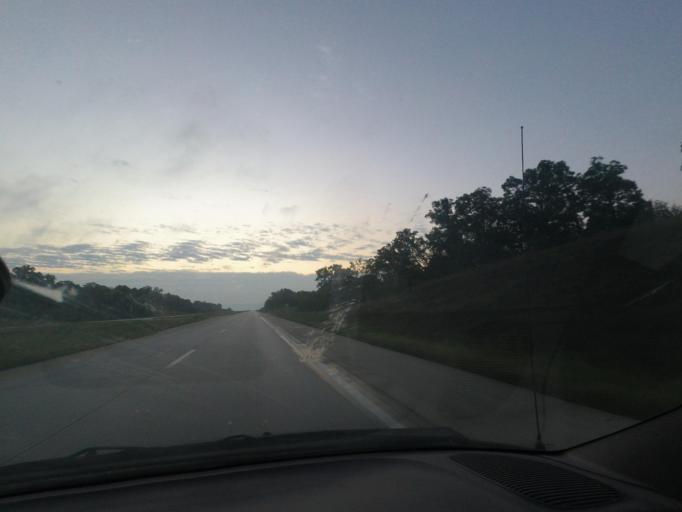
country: US
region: Missouri
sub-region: Linn County
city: Marceline
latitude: 39.7591
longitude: -92.8375
